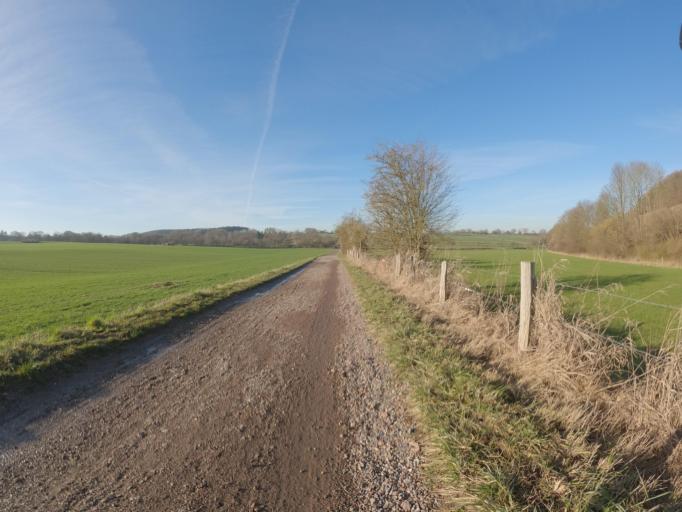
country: NL
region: Limburg
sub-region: Gemeente Vaals
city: Vaals
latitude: 50.7827
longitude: 6.0397
